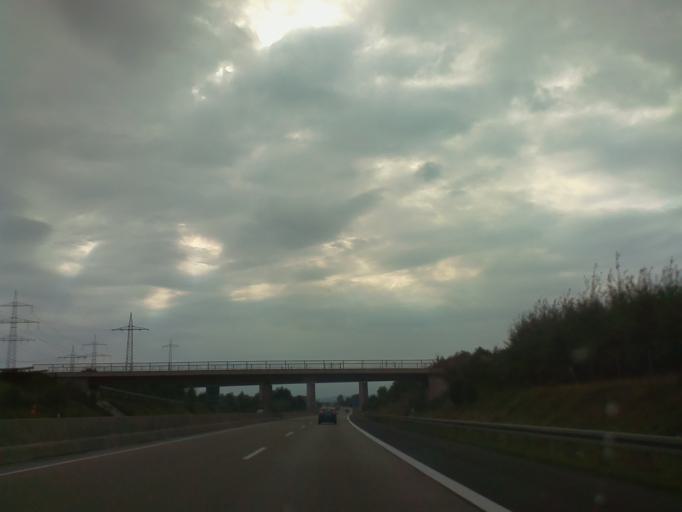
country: DE
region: Hesse
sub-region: Regierungsbezirk Kassel
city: Eichenzell
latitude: 50.4758
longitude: 9.6637
